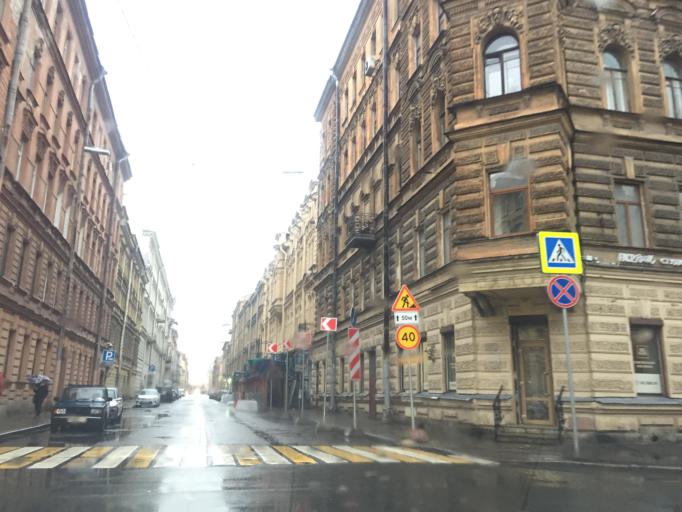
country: RU
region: St.-Petersburg
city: Centralniy
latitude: 59.9395
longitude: 30.3636
